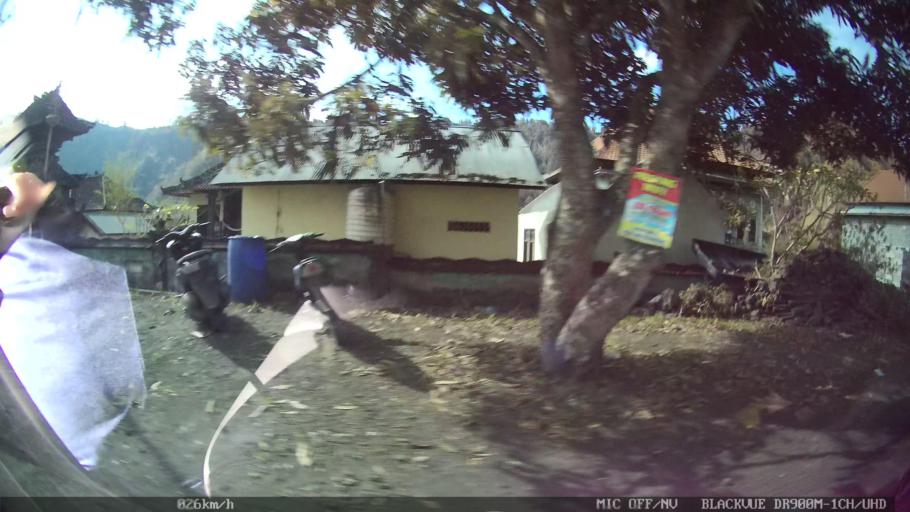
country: ID
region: Bali
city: Banjar Trunyan
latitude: -8.2148
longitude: 115.3720
